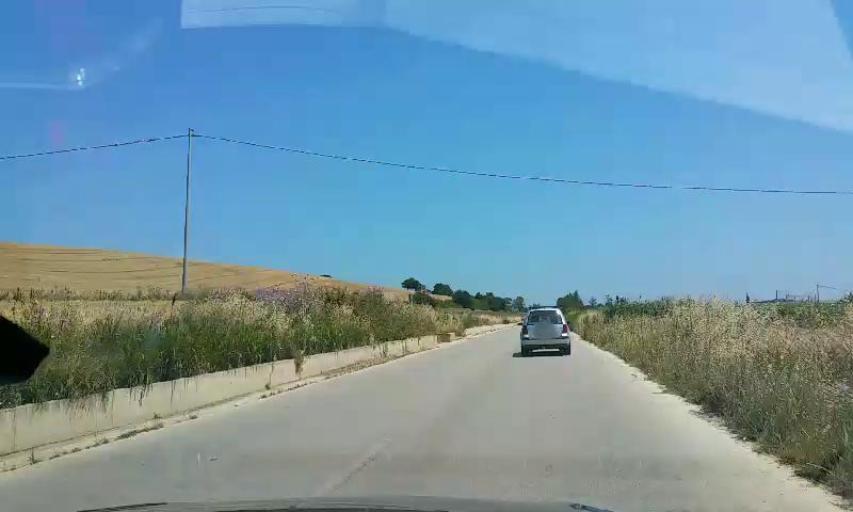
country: IT
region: Molise
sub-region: Provincia di Campobasso
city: Termoli
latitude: 42.0004
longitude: 14.9573
